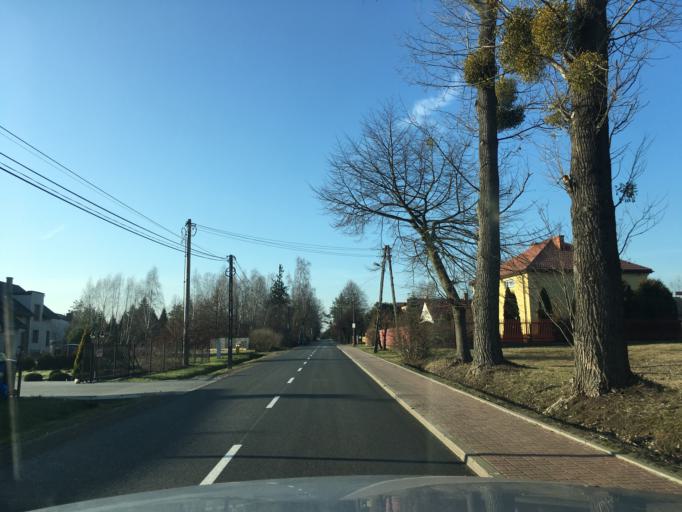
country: PL
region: Lodz Voivodeship
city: Zabia Wola
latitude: 52.0516
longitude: 20.7338
